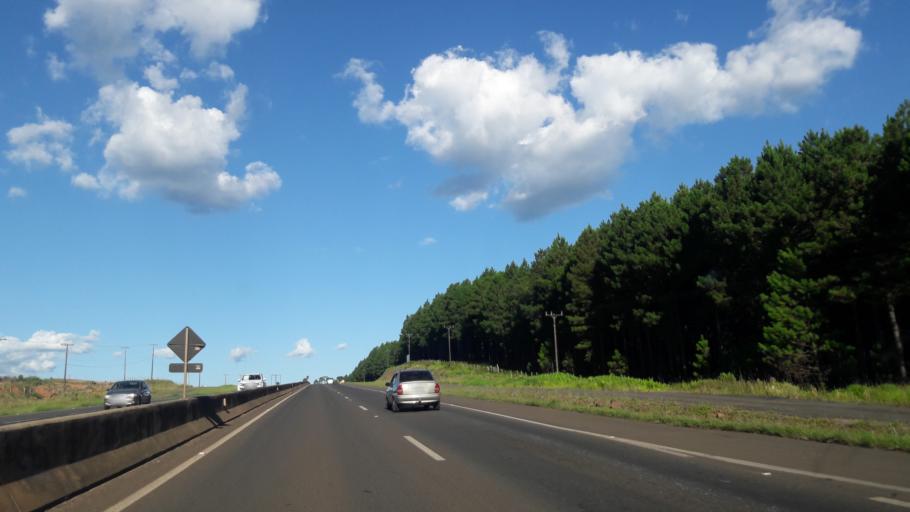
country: BR
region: Parana
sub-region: Guarapuava
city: Guarapuava
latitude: -25.3442
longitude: -51.4402
